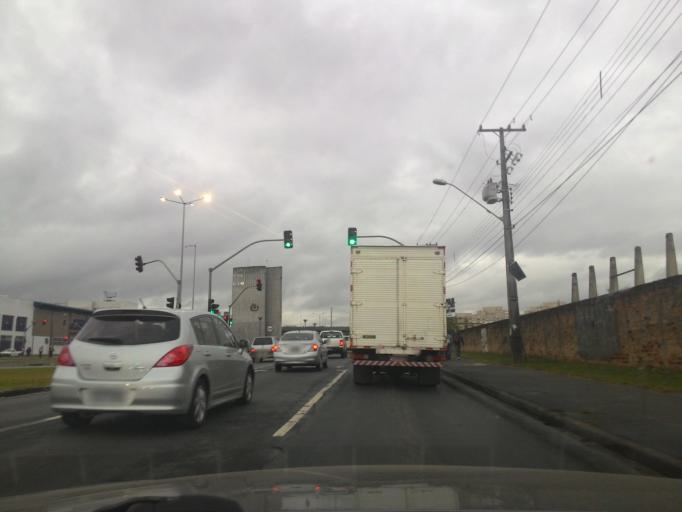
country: BR
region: Parana
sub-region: Curitiba
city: Curitiba
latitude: -25.4979
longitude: -49.2768
